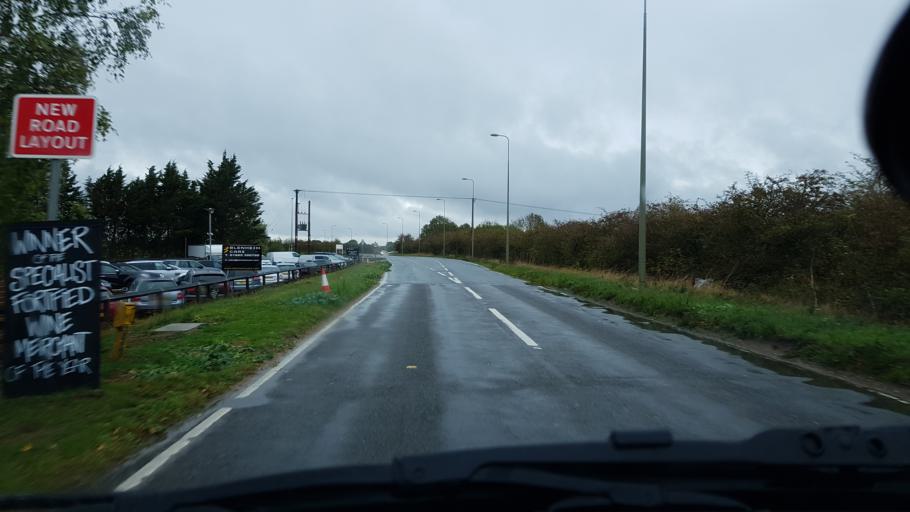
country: GB
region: England
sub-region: Oxfordshire
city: Ducklington
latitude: 51.7399
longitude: -1.4447
